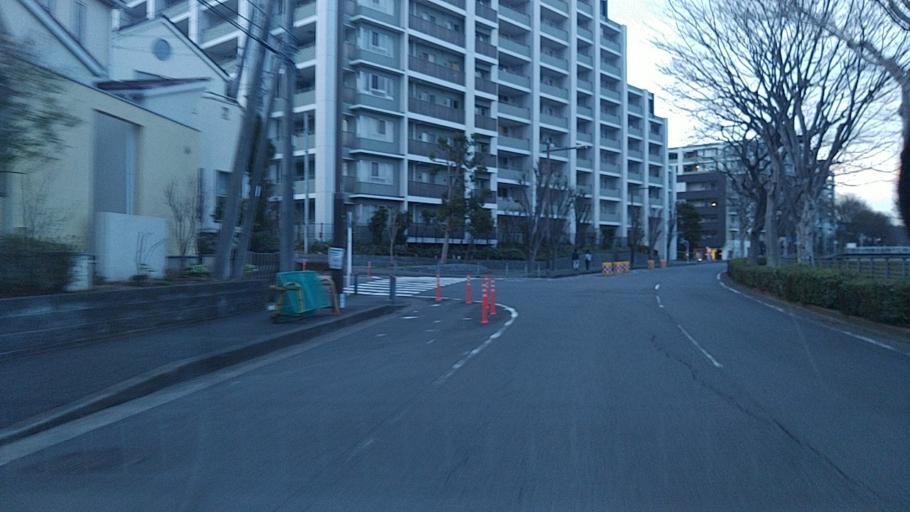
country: JP
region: Kanagawa
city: Fujisawa
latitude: 35.4118
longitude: 139.4881
